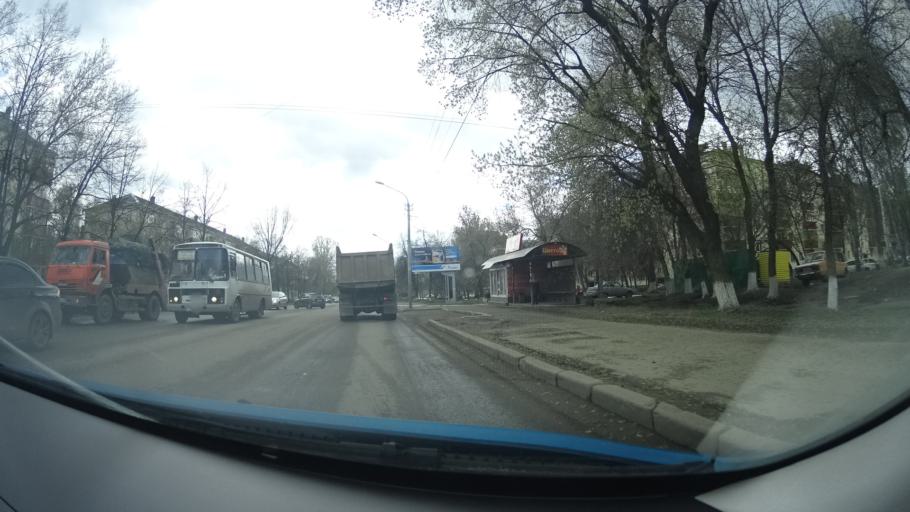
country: RU
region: Bashkortostan
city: Ufa
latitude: 54.8130
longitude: 56.0893
